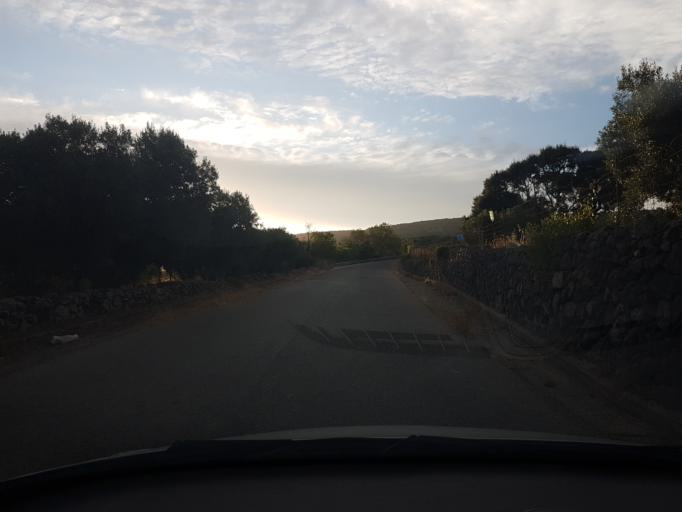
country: IT
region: Sardinia
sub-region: Provincia di Oristano
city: Seneghe
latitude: 40.0987
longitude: 8.6219
